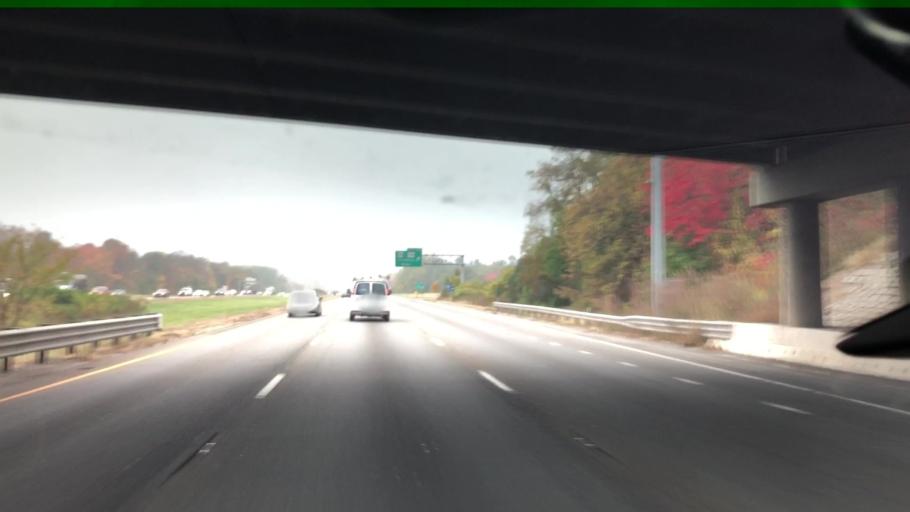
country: US
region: Massachusetts
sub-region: Middlesex County
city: Littleton Common
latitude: 42.5397
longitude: -71.4932
